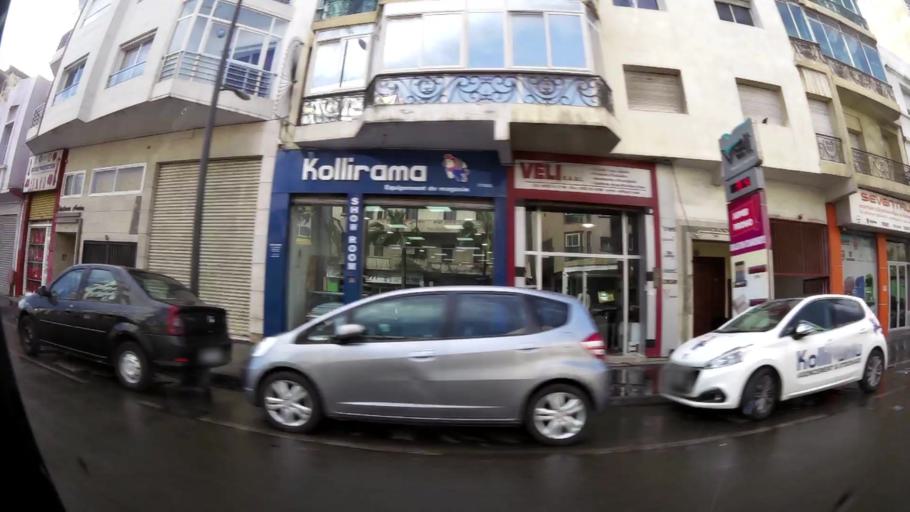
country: MA
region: Grand Casablanca
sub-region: Casablanca
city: Casablanca
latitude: 33.6024
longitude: -7.5830
